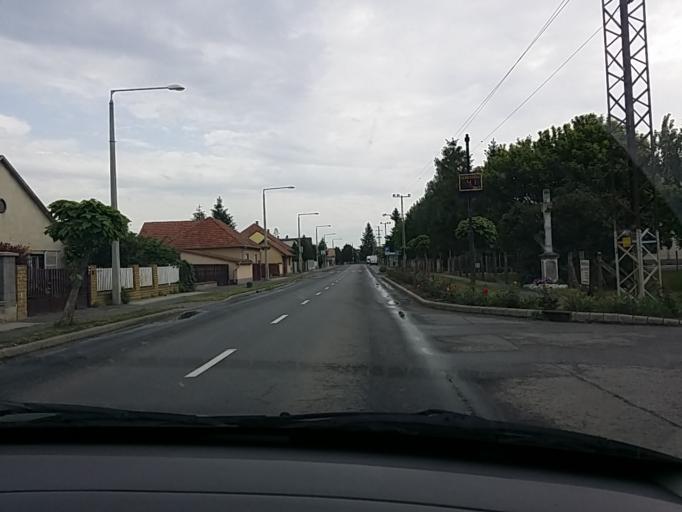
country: HU
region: Borsod-Abauj-Zemplen
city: Tokaj
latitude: 48.1070
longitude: 21.4046
